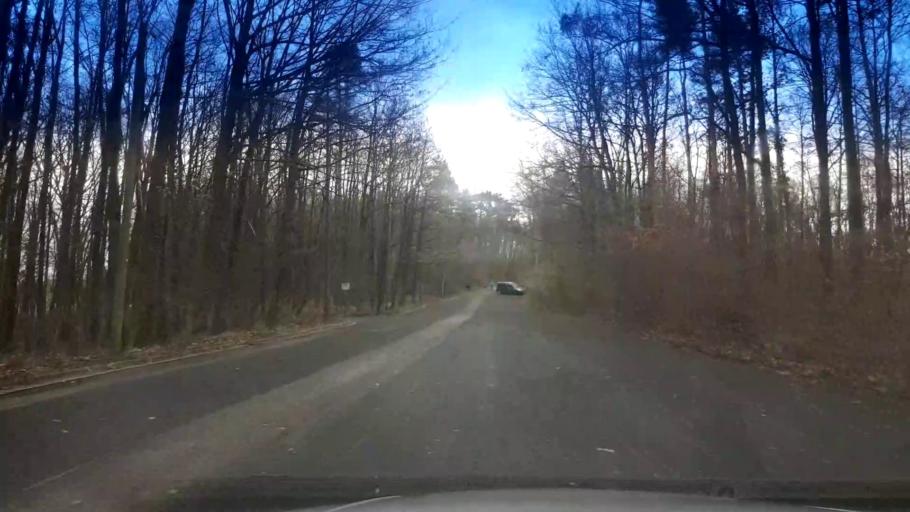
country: DE
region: Bavaria
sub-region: Upper Franconia
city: Bischberg
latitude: 49.8965
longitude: 10.8561
